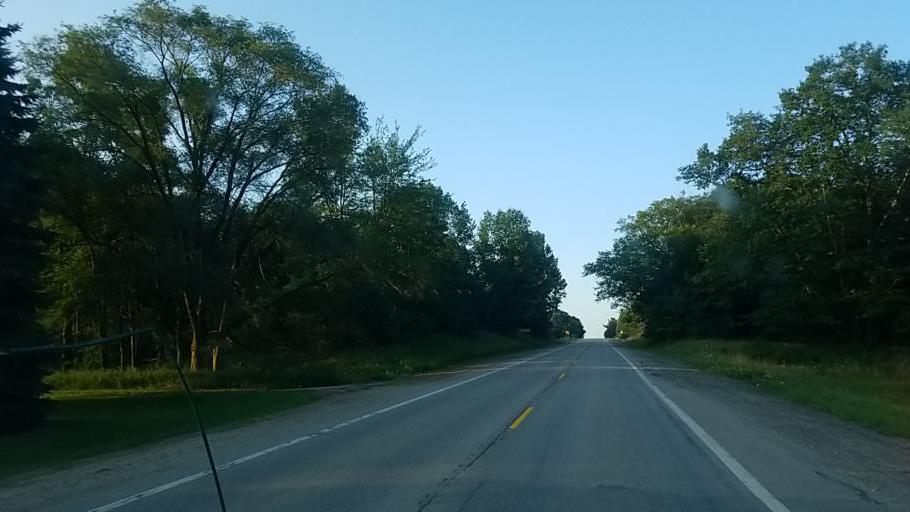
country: US
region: Michigan
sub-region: Isabella County
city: Lake Isabella
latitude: 43.6823
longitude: -85.1465
